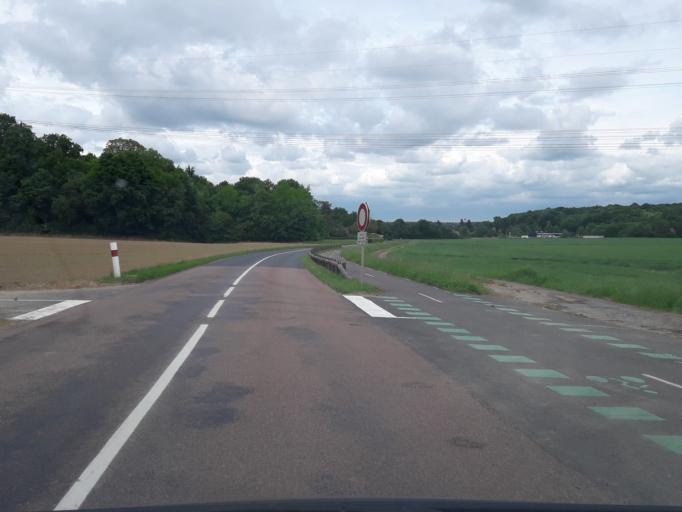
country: FR
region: Ile-de-France
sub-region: Departement de l'Essonne
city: Boissy-le-Cutte
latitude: 48.4498
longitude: 2.3069
